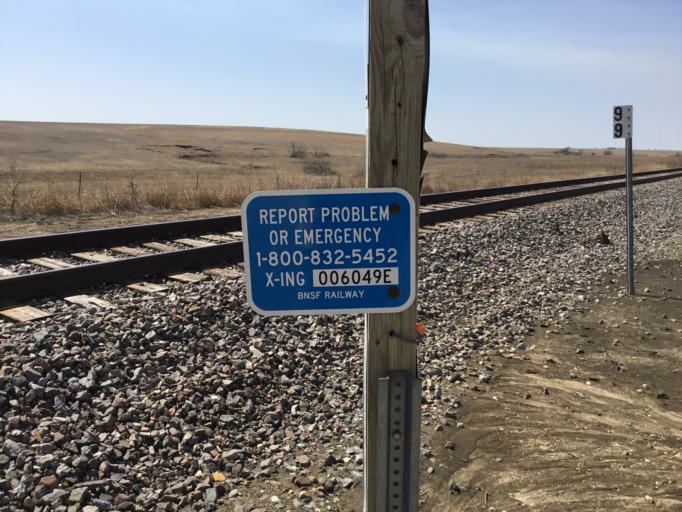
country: US
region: Kansas
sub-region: Lyon County
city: Emporia
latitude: 38.5066
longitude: -95.9963
